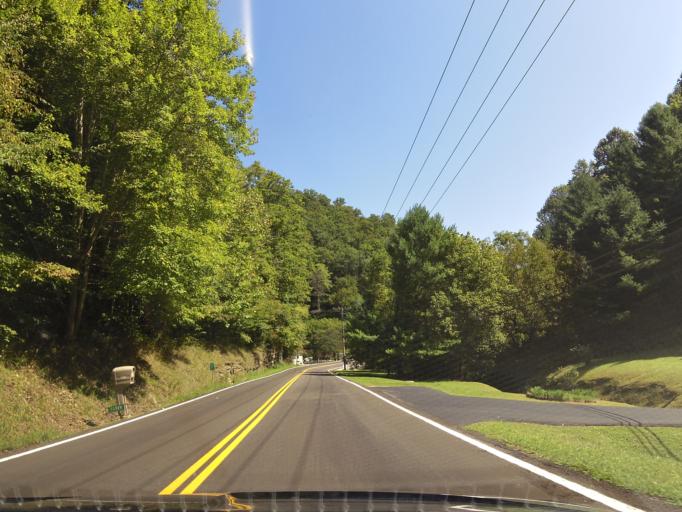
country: US
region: Kentucky
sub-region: Clay County
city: Manchester
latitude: 37.1158
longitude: -83.6488
